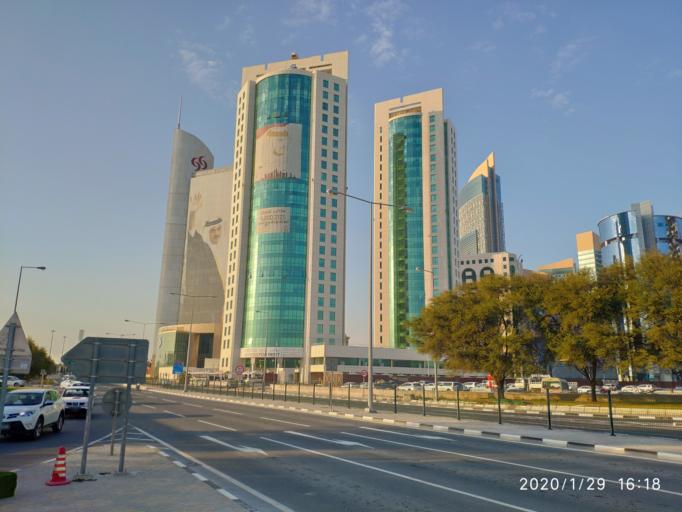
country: QA
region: Baladiyat ad Dawhah
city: Doha
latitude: 25.3116
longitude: 51.5198
